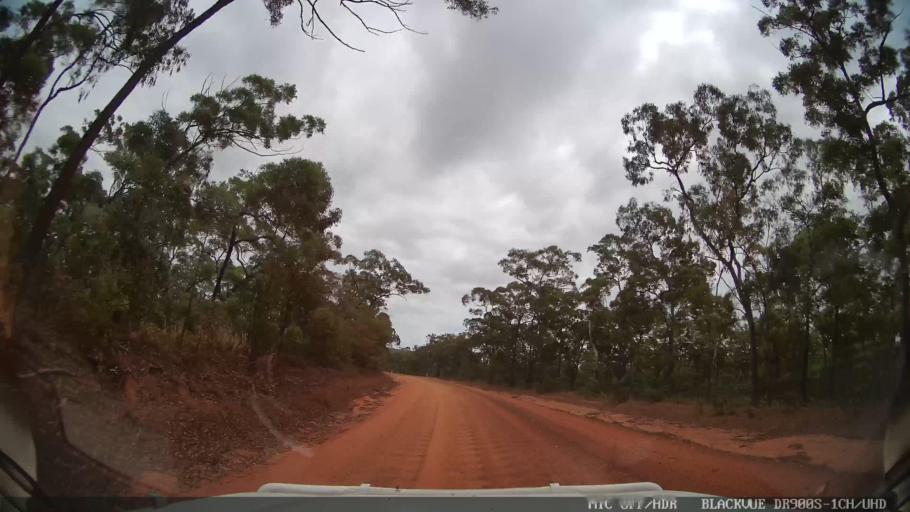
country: AU
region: Queensland
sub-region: Cook
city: Cooktown
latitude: -15.2640
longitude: 144.9560
